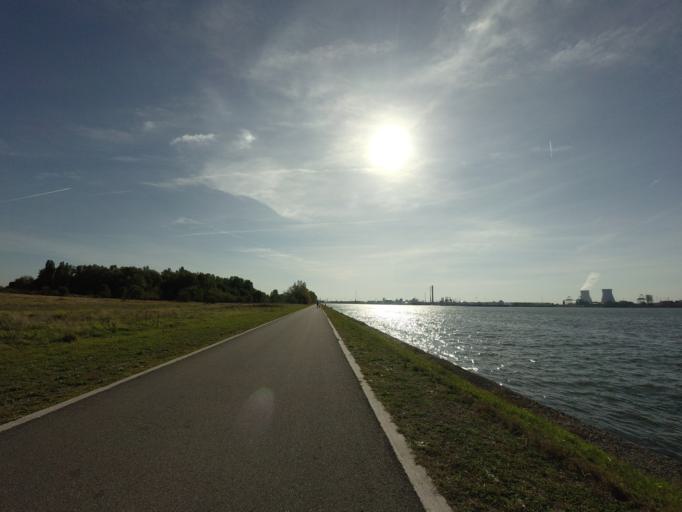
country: BE
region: Flanders
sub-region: Provincie Antwerpen
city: Stabroek
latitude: 51.3505
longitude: 4.3020
